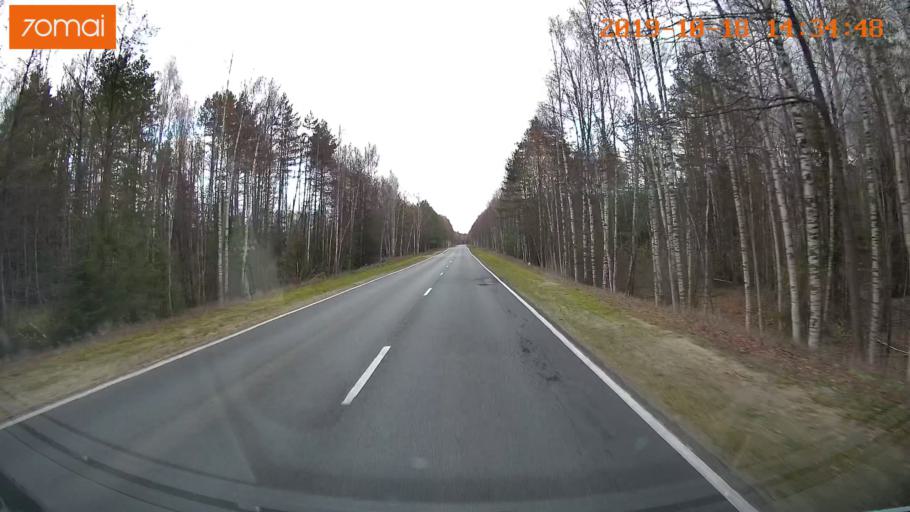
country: RU
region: Vladimir
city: Velikodvorskiy
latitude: 55.2161
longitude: 40.6232
